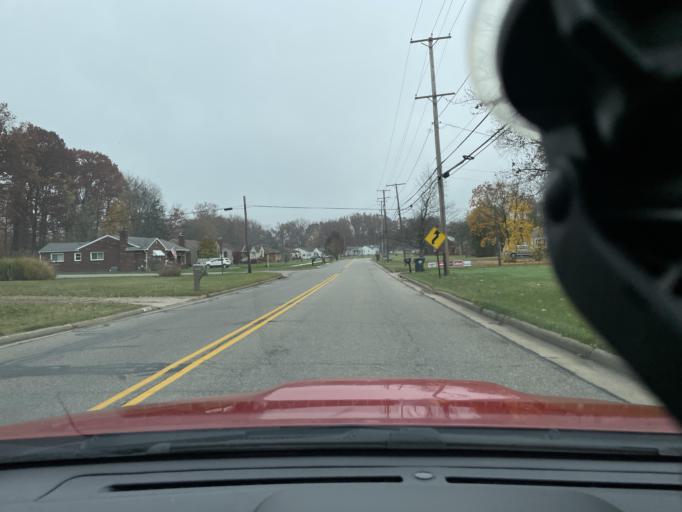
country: US
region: Ohio
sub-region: Mahoning County
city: Austintown
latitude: 41.1058
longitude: -80.7476
